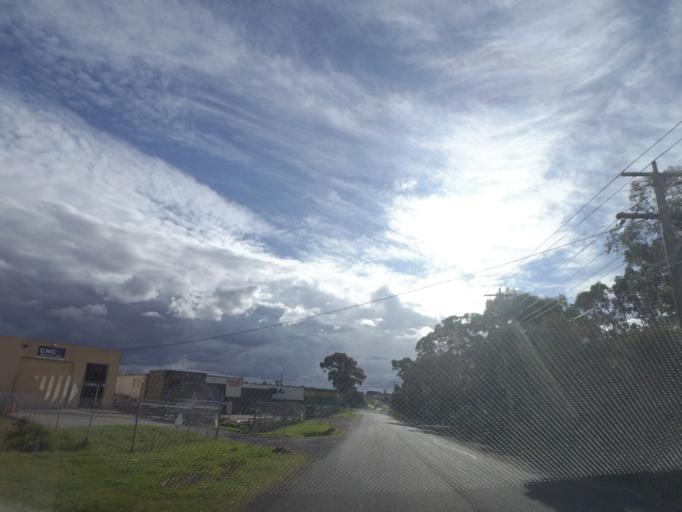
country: AU
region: Victoria
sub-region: Yarra Ranges
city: Lilydale
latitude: -37.7477
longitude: 145.3558
